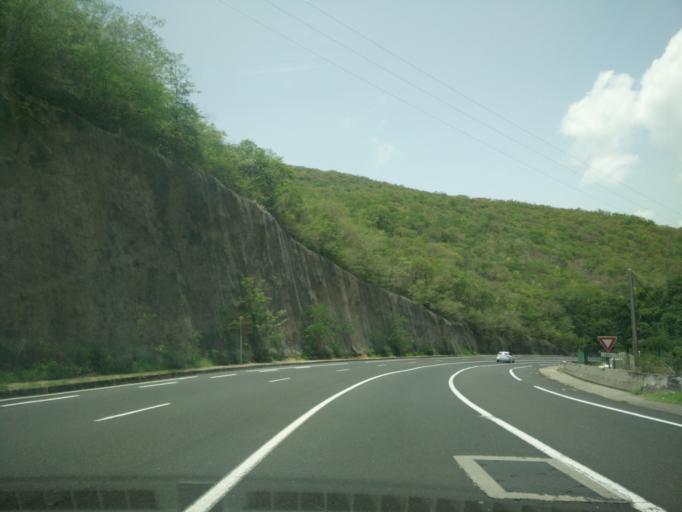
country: MQ
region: Martinique
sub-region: Martinique
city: Saint-Pierre
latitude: 14.6628
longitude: -61.1546
